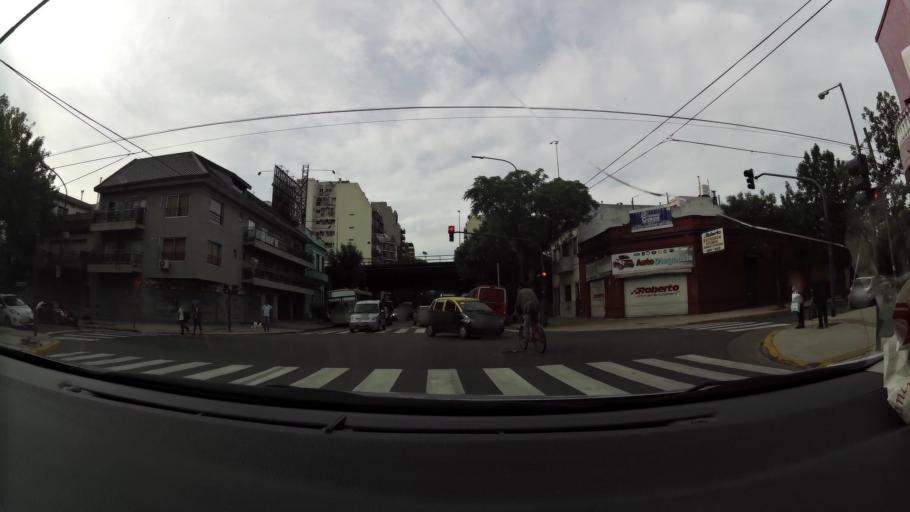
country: AR
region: Buenos Aires F.D.
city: Villa Santa Rita
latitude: -34.6306
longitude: -58.4332
